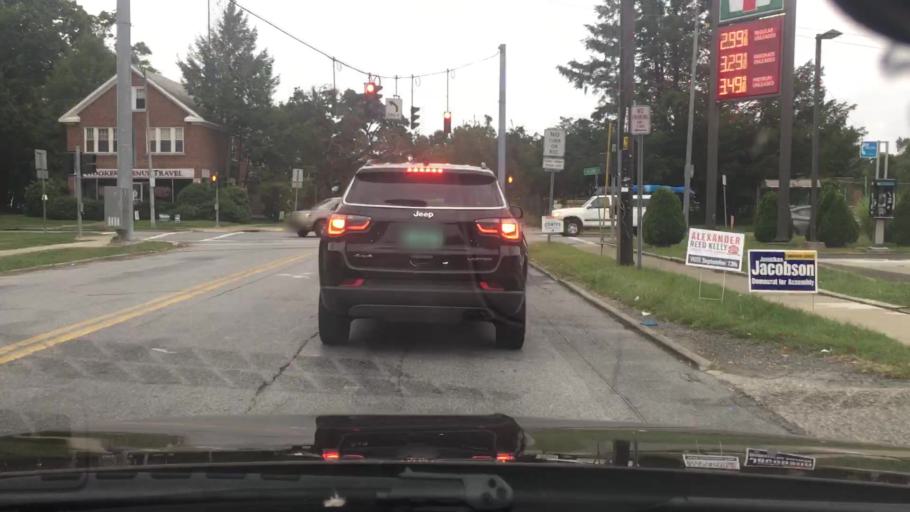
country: US
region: New York
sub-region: Dutchess County
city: Arlington
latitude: 41.6862
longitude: -73.9096
